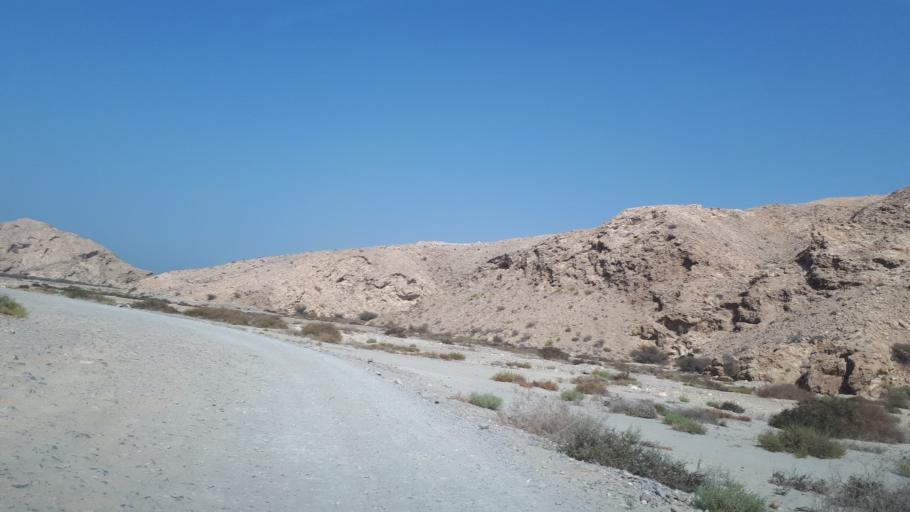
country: OM
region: Muhafazat Masqat
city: Muscat
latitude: 23.5381
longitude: 58.6549
